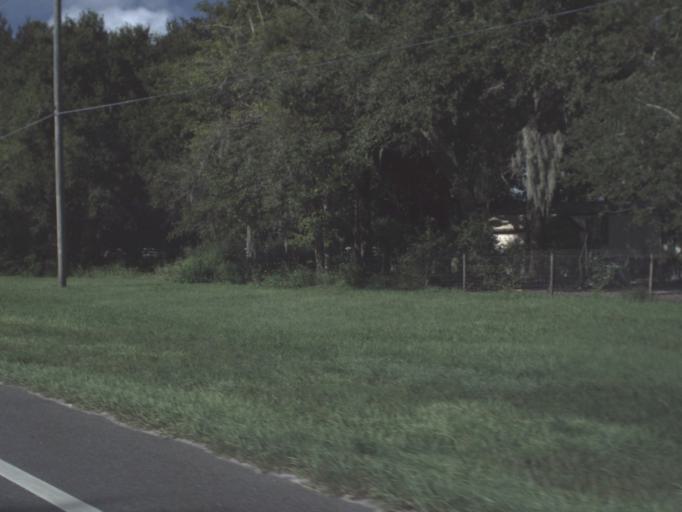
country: US
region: Florida
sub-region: Polk County
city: Polk City
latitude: 28.1698
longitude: -81.8556
